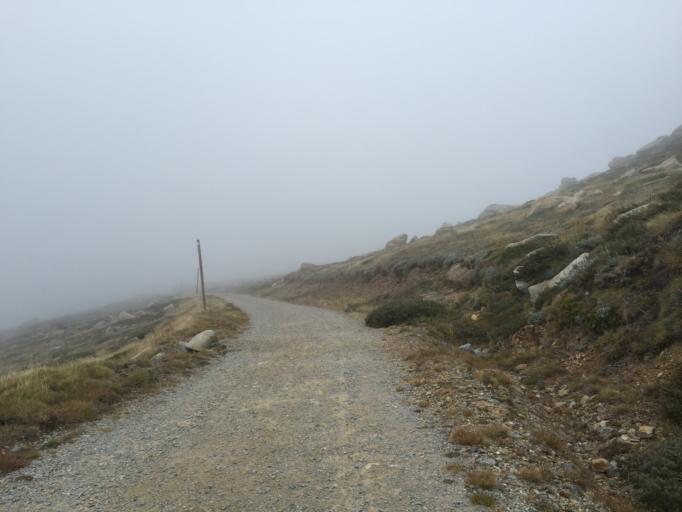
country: AU
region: New South Wales
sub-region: Snowy River
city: Jindabyne
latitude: -36.4503
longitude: 148.2798
